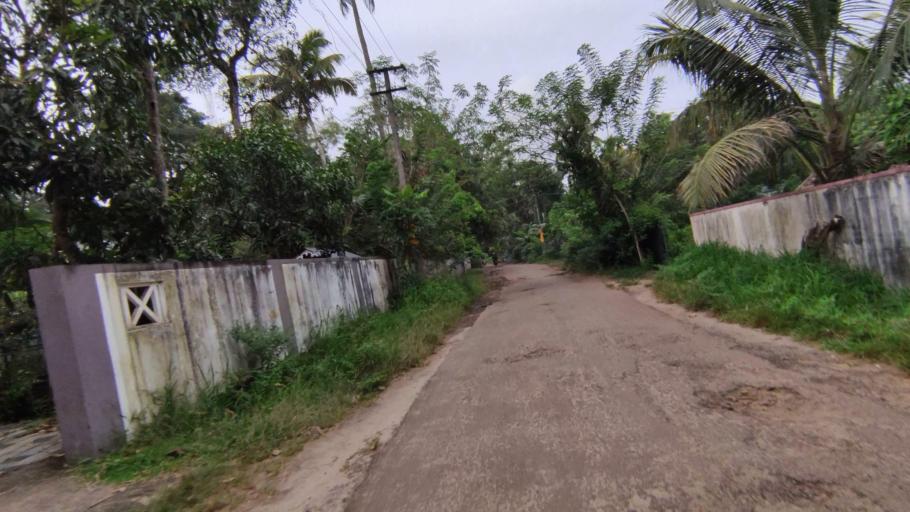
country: IN
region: Kerala
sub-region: Alappuzha
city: Shertallai
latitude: 9.6183
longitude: 76.3564
